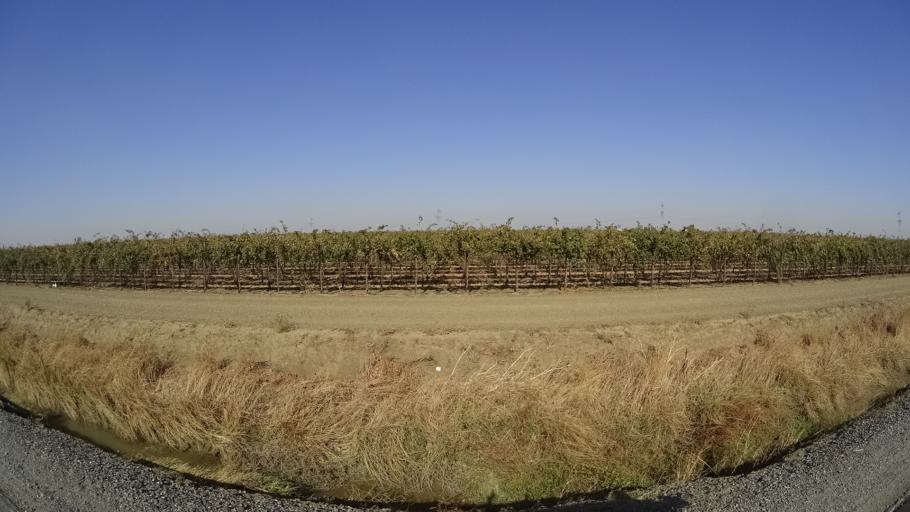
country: US
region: California
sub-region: Yolo County
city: Esparto
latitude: 38.7225
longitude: -121.9668
